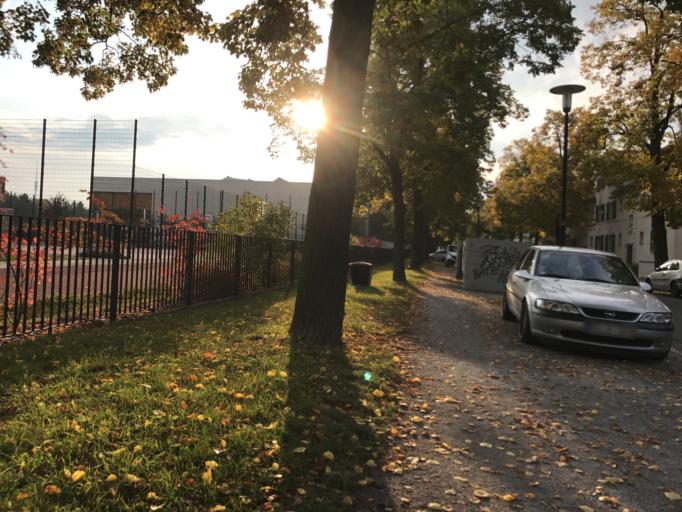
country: DE
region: Saxony
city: Albertstadt
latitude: 51.0370
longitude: 13.7935
